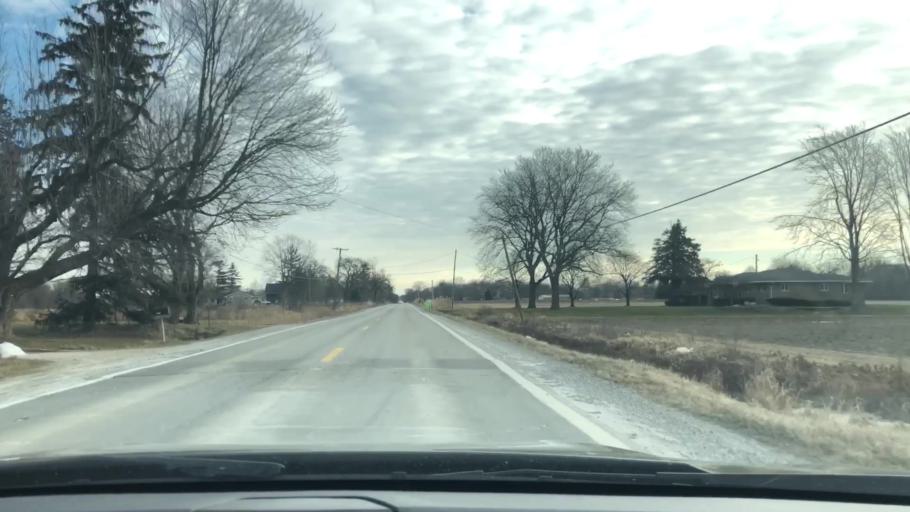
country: US
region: Michigan
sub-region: Macomb County
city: New Haven
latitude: 42.7158
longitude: -82.9137
